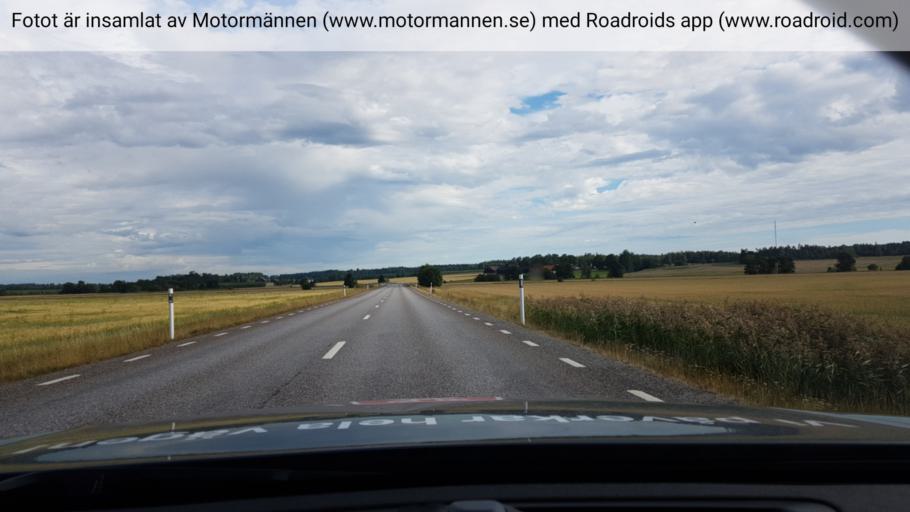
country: SE
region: Uppsala
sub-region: Heby Kommun
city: Morgongava
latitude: 59.8247
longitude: 16.9252
